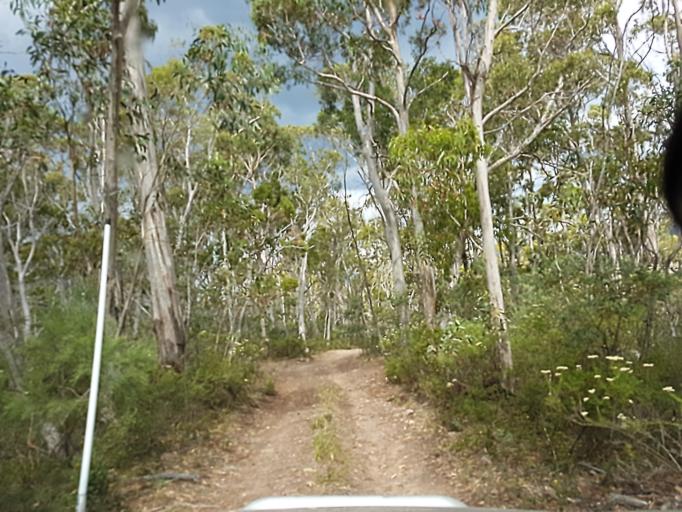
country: AU
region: New South Wales
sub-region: Snowy River
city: Jindabyne
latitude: -36.8793
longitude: 148.2019
